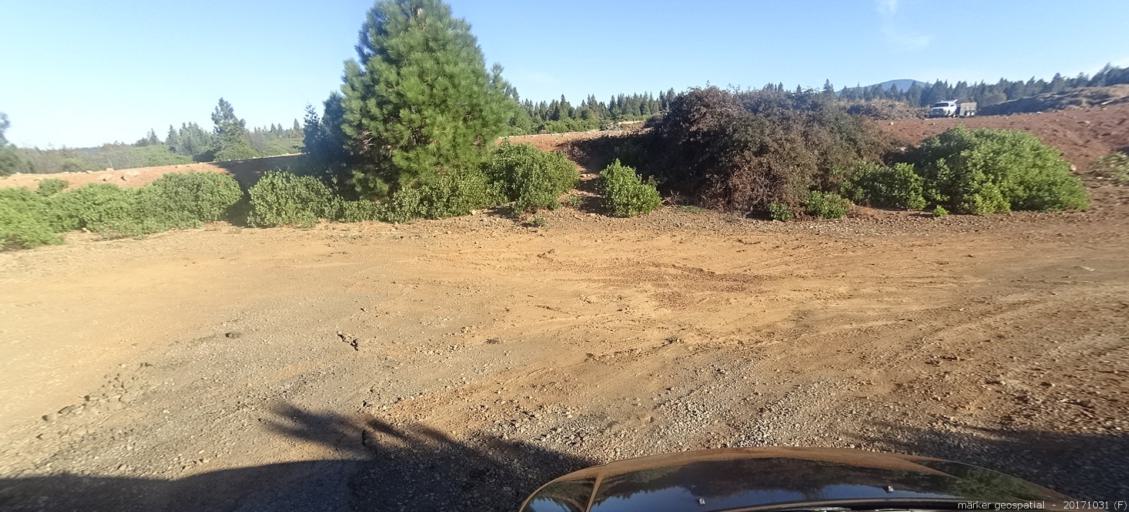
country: US
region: California
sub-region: Shasta County
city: Shingletown
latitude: 40.5181
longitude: -121.8055
